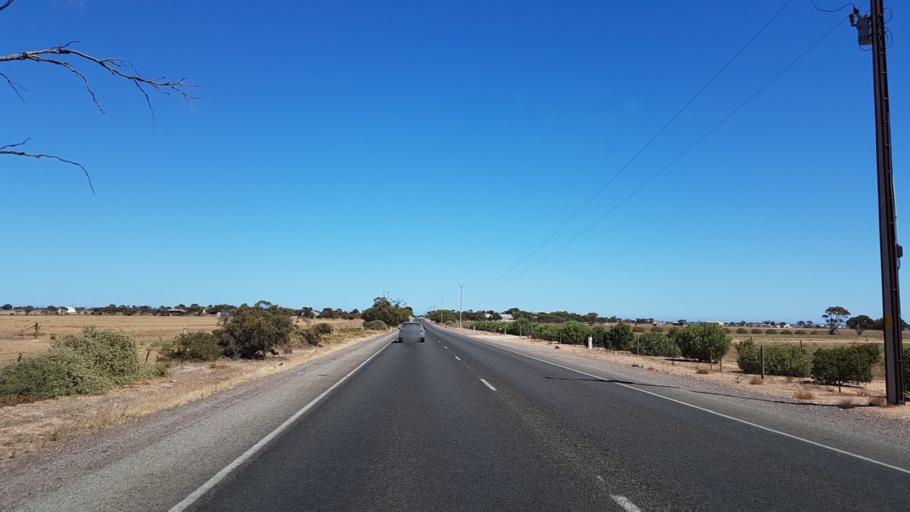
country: AU
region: South Australia
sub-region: Copper Coast
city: Wallaroo
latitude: -33.9443
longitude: 137.6609
